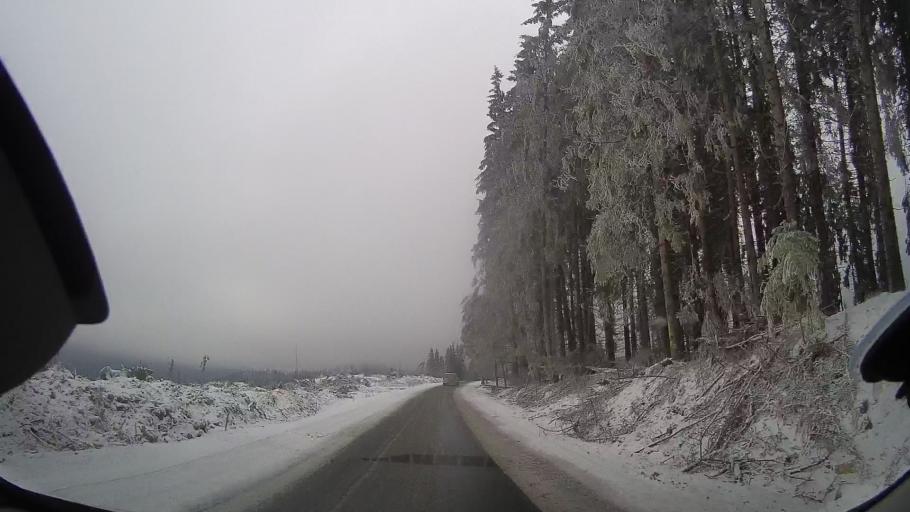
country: RO
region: Cluj
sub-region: Comuna Belis
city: Belis
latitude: 46.6421
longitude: 23.0417
